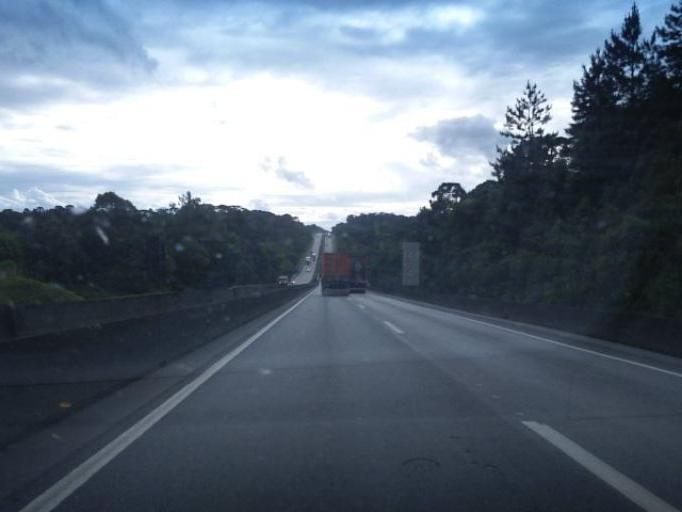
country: BR
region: Parana
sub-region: Campina Grande Do Sul
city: Campina Grande do Sul
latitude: -25.3036
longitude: -48.9667
